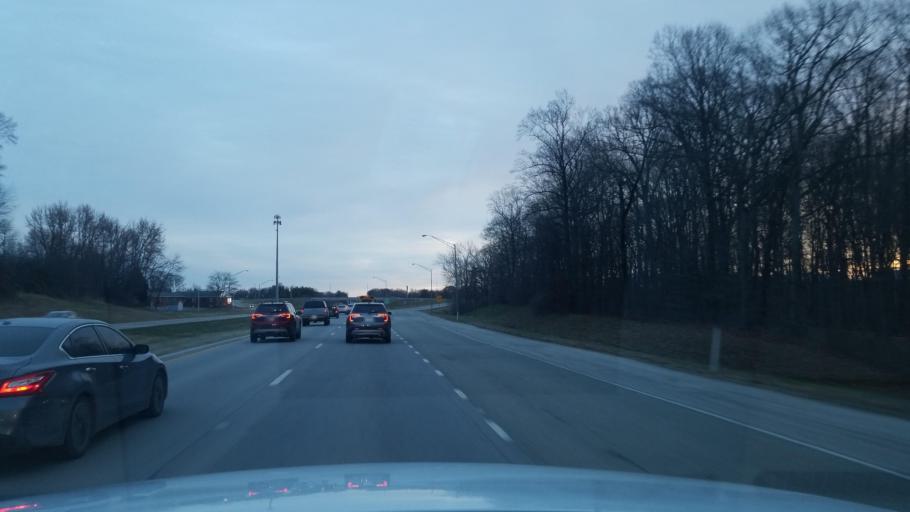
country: US
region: Indiana
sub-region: Vanderburgh County
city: Evansville
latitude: 37.9657
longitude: -87.6828
